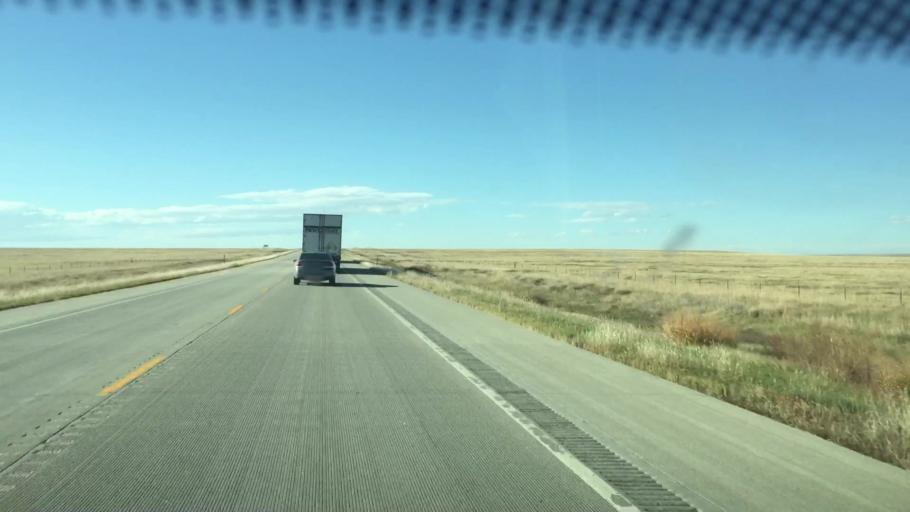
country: US
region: Colorado
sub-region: Lincoln County
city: Hugo
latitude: 38.9202
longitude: -103.1845
